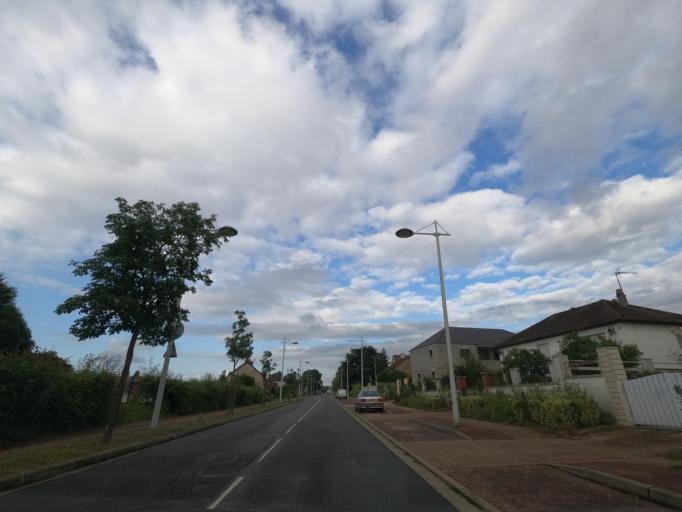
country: FR
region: Haute-Normandie
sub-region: Departement de la Seine-Maritime
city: Grand-Couronne
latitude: 49.3523
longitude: 1.0001
